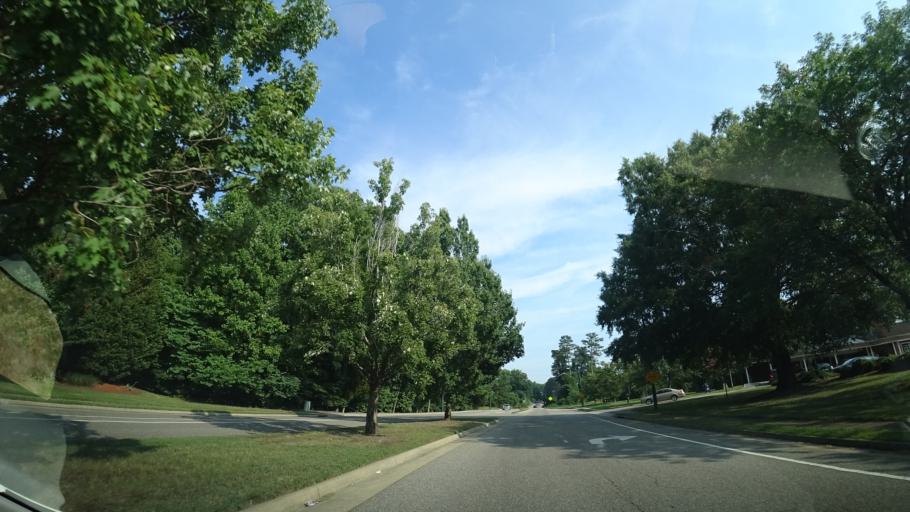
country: US
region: Virginia
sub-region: City of Williamsburg
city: Williamsburg
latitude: 37.2861
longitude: -76.6858
